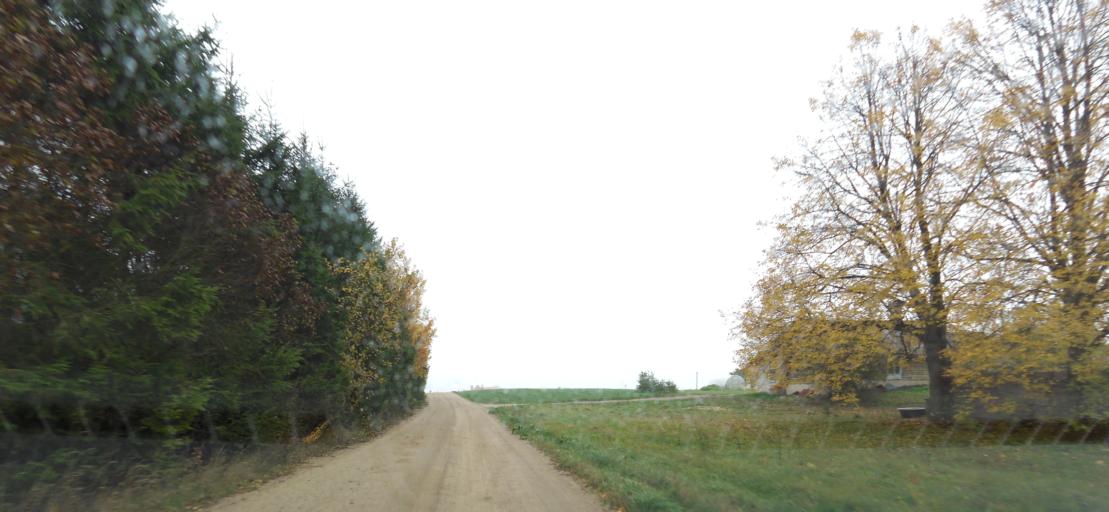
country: LT
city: Skaidiskes
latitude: 54.6196
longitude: 25.4707
